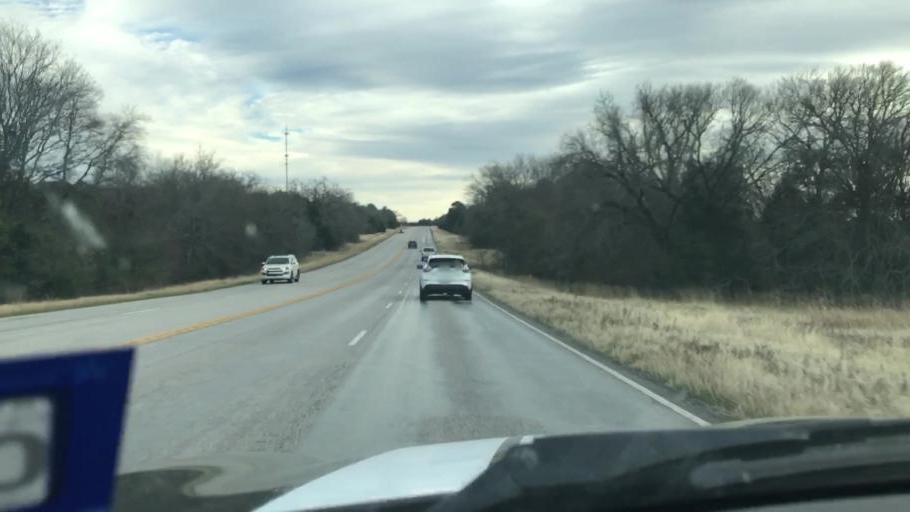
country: US
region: Texas
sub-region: Bastrop County
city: Camp Swift
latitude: 30.2560
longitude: -97.2271
